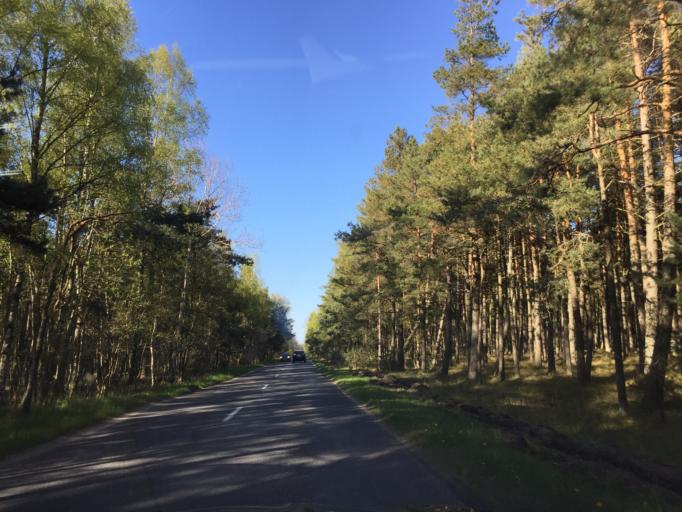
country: LT
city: Nida
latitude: 55.2074
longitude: 20.8760
